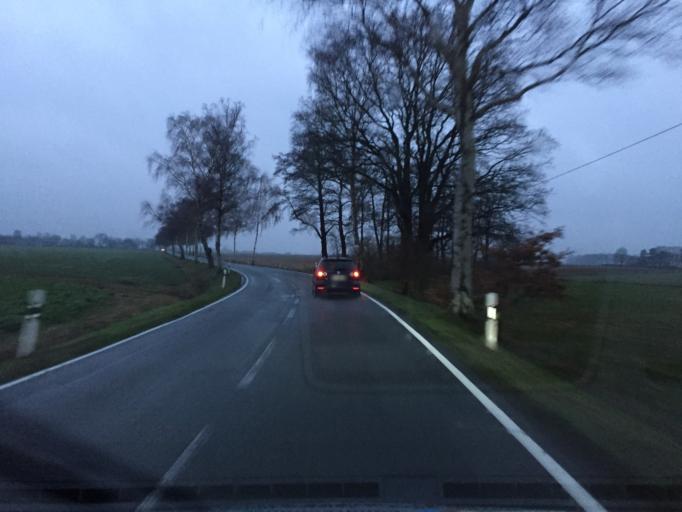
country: DE
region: Lower Saxony
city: Sustedt
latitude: 52.8687
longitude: 8.8605
